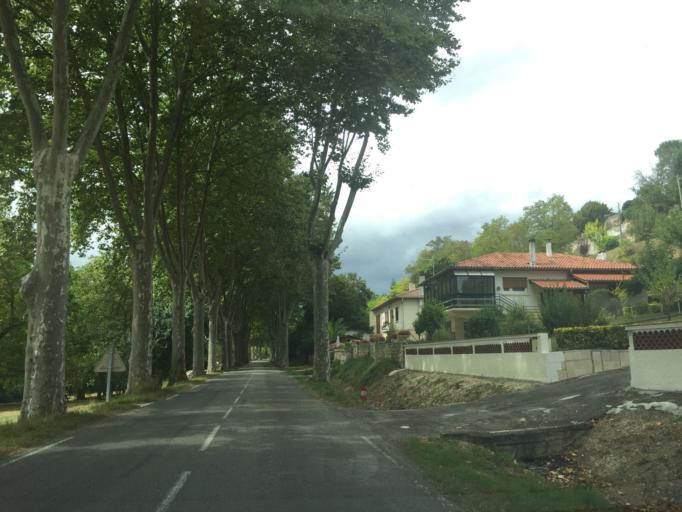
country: FR
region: Midi-Pyrenees
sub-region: Departement du Gers
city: Valence-sur-Baise
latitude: 43.8807
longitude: 0.3803
